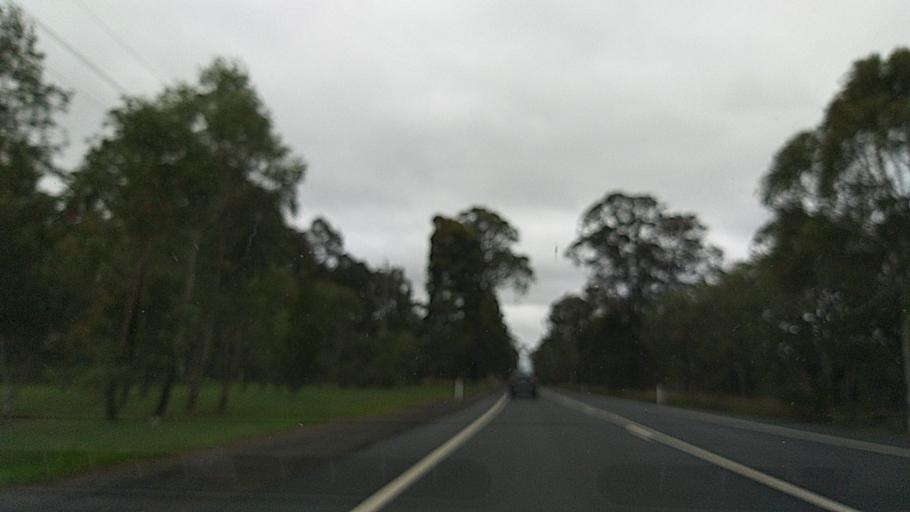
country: AU
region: New South Wales
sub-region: Hawkesbury
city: South Windsor
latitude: -33.6567
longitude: 150.7700
